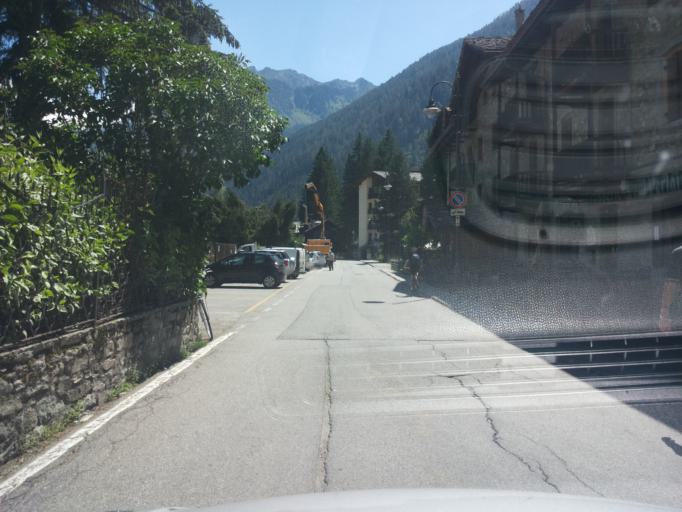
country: IT
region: Aosta Valley
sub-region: Valle d'Aosta
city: Gressoney-Saint-Jean
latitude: 45.7782
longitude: 7.8255
